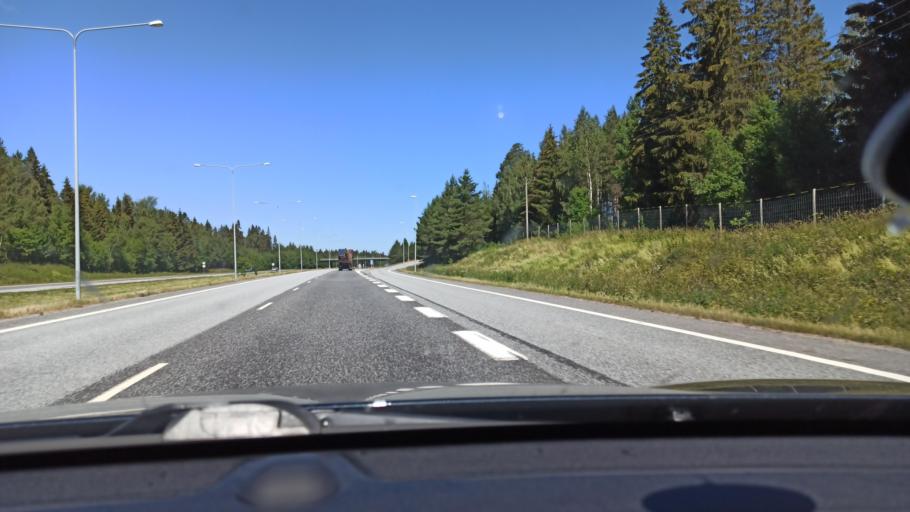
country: FI
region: Ostrobothnia
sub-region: Vaasa
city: Ristinummi
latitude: 63.0501
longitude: 21.7184
